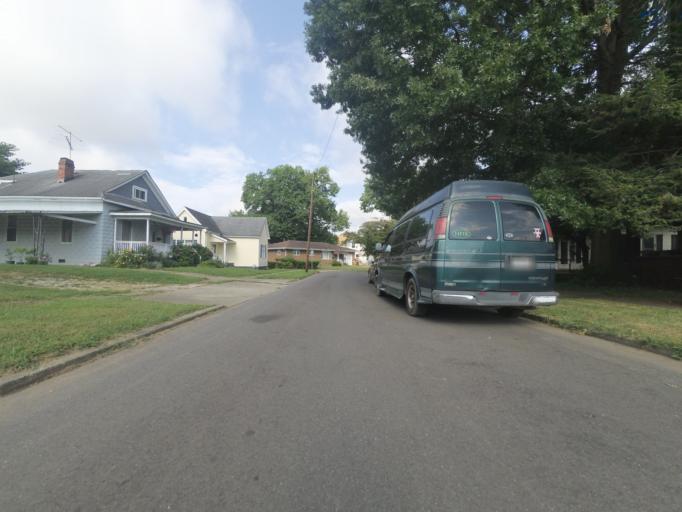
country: US
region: West Virginia
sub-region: Cabell County
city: Huntington
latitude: 38.4330
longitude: -82.4030
